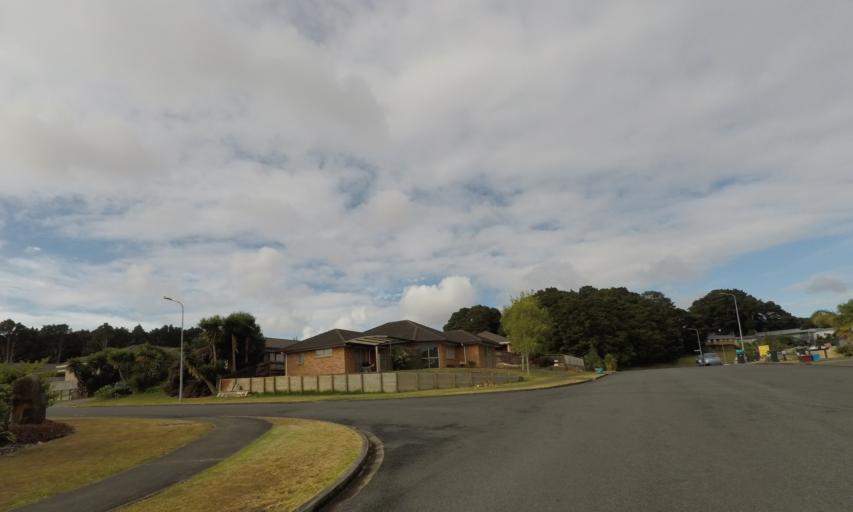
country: NZ
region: Northland
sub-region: Whangarei
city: Whangarei
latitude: -35.6726
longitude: 174.3149
